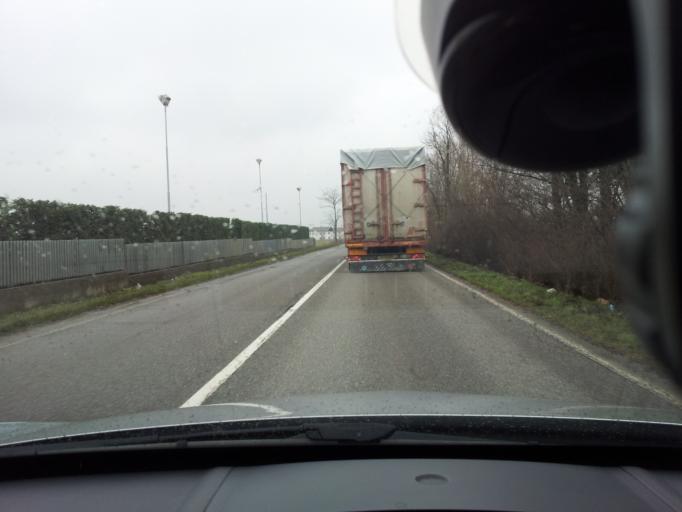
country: IT
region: Lombardy
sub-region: Provincia di Bergamo
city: Calcinate
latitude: 45.6120
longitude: 9.7883
